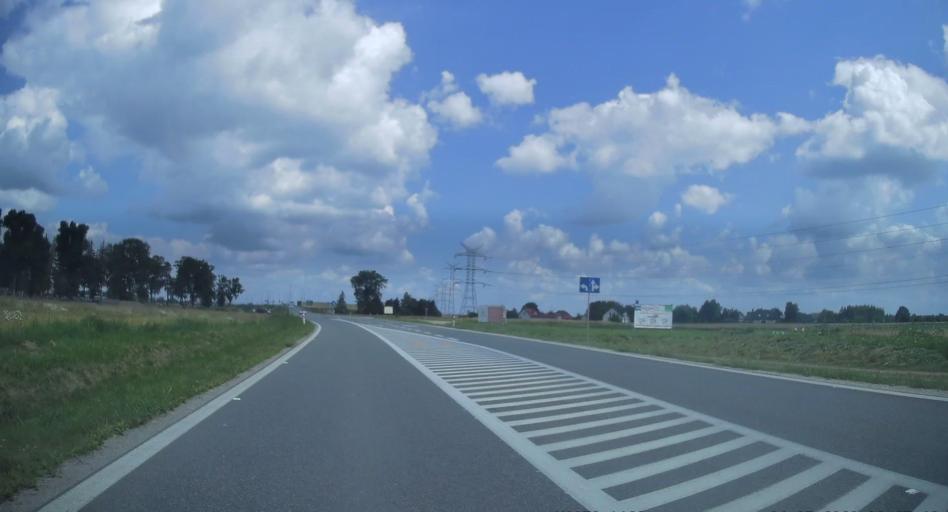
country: PL
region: Lesser Poland Voivodeship
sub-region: Powiat tarnowski
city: Wojnicz
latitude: 49.9582
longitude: 20.8521
